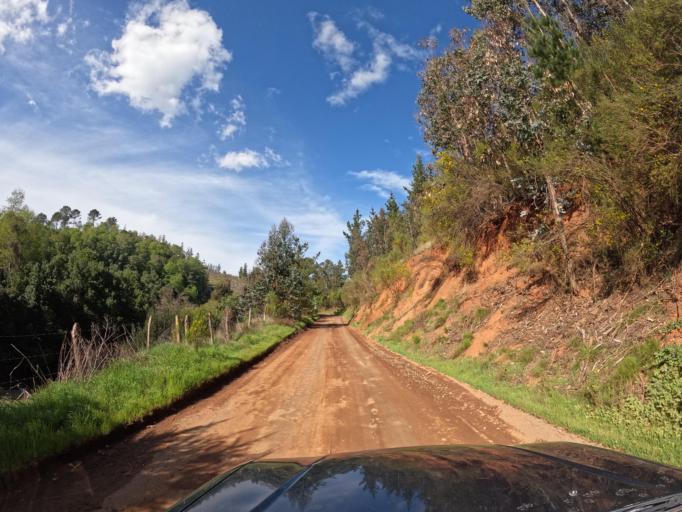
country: CL
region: Biobio
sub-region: Provincia de Concepcion
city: Chiguayante
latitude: -37.0738
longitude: -72.8401
